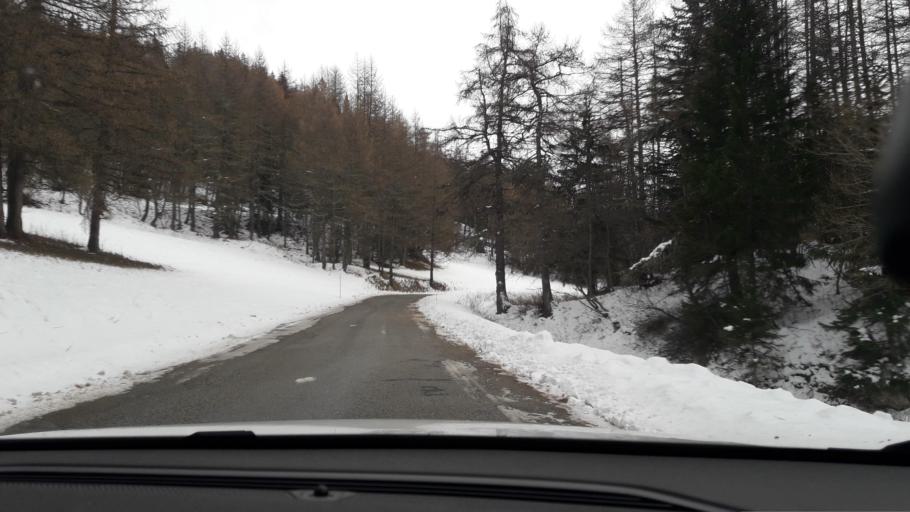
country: FR
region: Rhone-Alpes
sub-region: Departement de la Savoie
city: Saint-Michel-de-Maurienne
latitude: 45.2182
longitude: 6.4231
